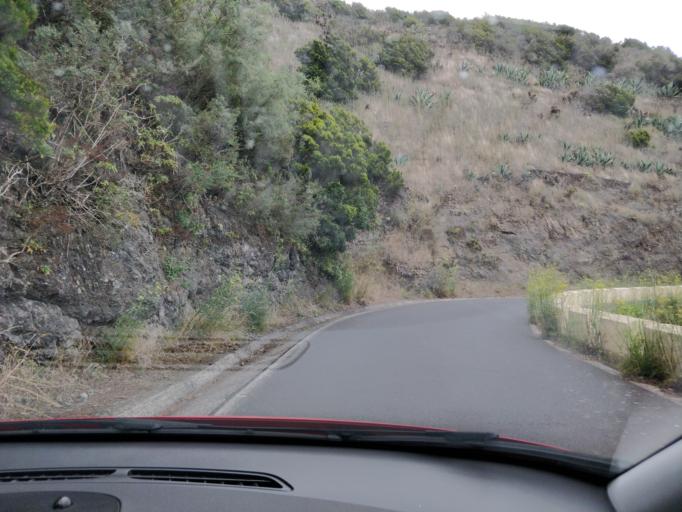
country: ES
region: Canary Islands
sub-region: Provincia de Santa Cruz de Tenerife
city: Tanque
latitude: 28.3258
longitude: -16.8540
